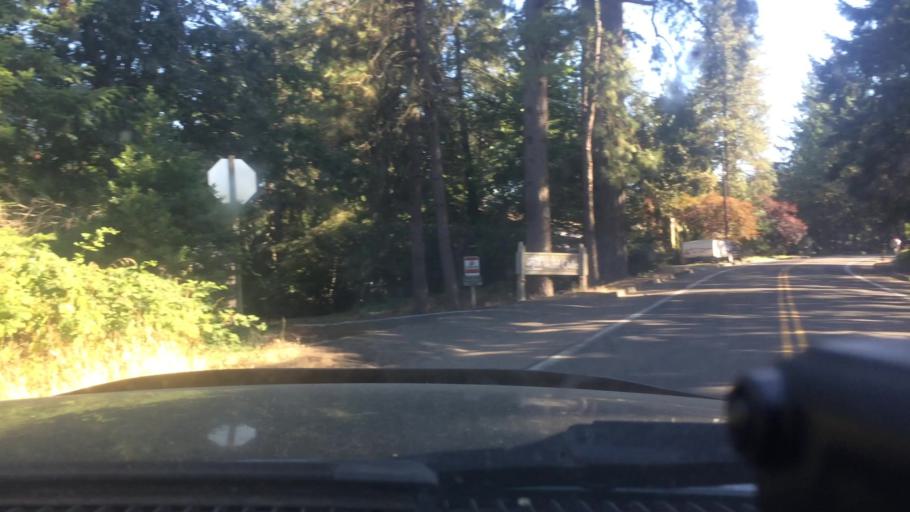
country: US
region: Oregon
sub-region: Lane County
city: Eugene
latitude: 44.0071
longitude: -123.0791
